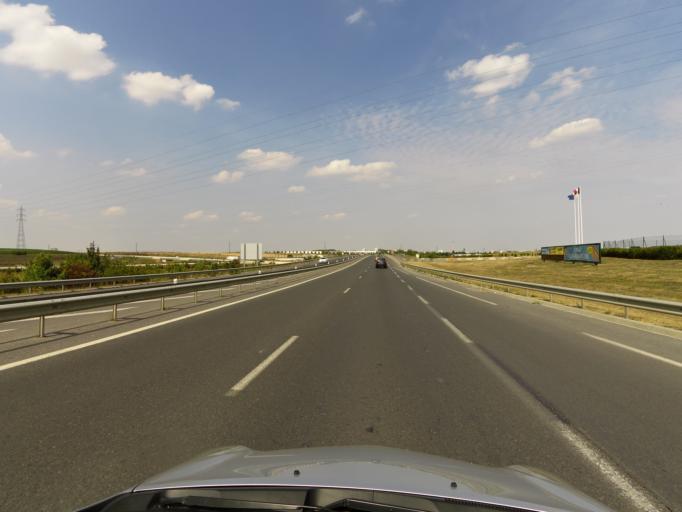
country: FR
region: Champagne-Ardenne
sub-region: Departement de la Marne
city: Bezannes
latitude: 49.2043
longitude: 4.0113
